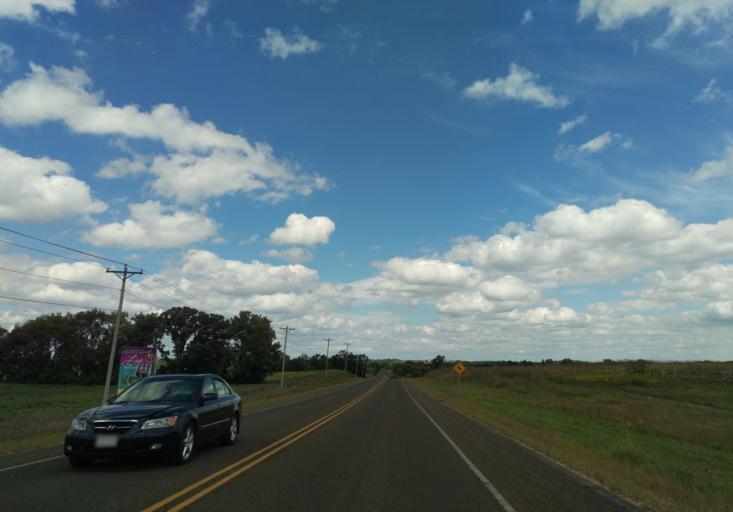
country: US
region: Wisconsin
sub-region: Dane County
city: Shorewood Hills
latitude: 43.1324
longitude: -89.4421
